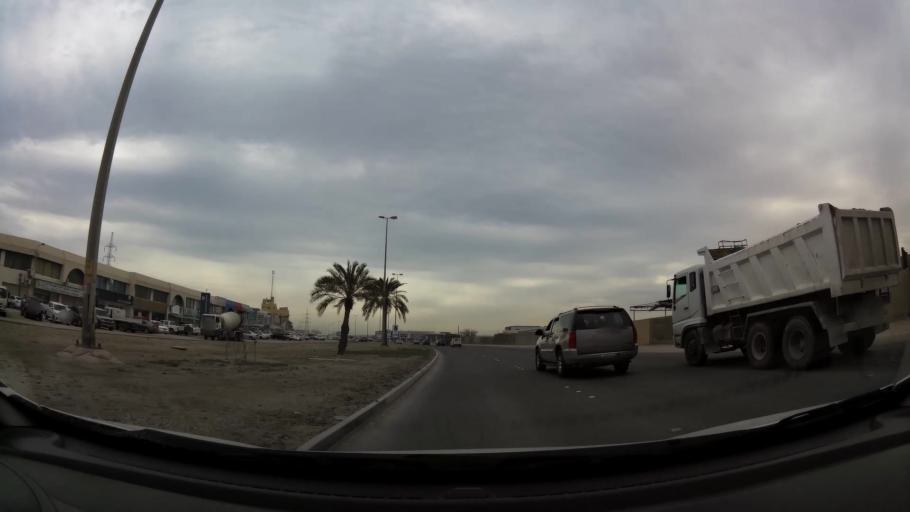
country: BH
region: Northern
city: Sitrah
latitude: 26.1580
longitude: 50.6063
